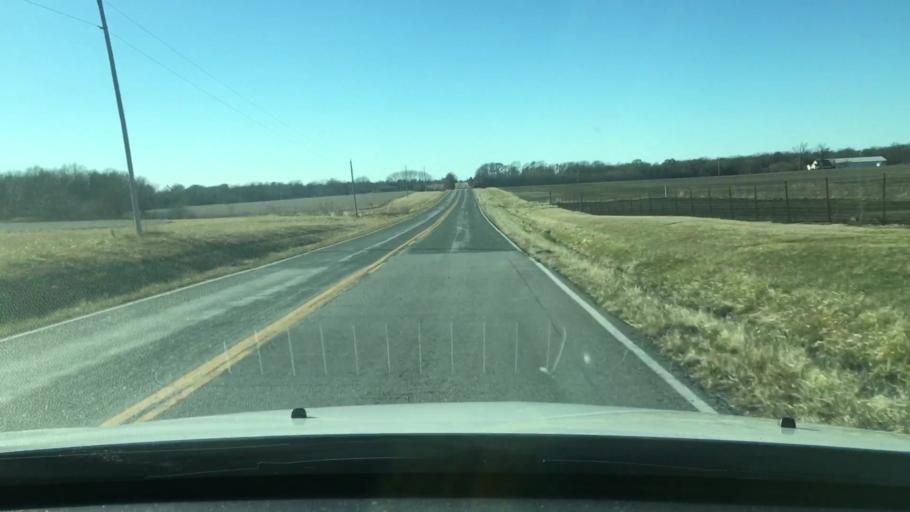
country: US
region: Missouri
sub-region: Audrain County
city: Vandalia
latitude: 39.2812
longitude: -91.6569
